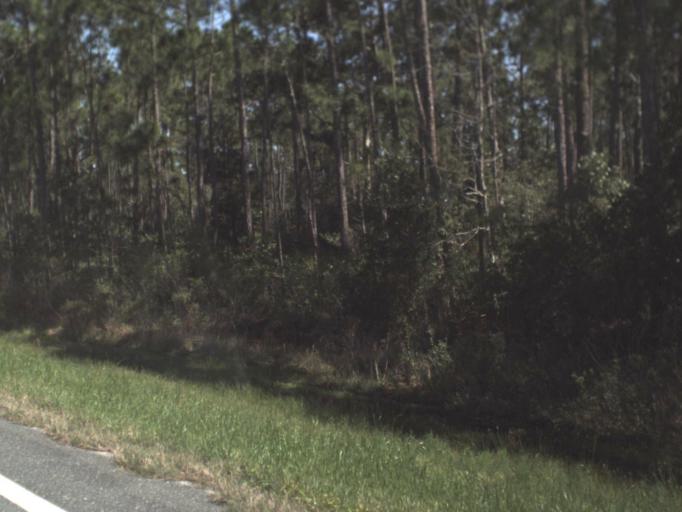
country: US
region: Florida
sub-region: Wakulla County
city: Crawfordville
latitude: 30.0027
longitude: -84.3975
